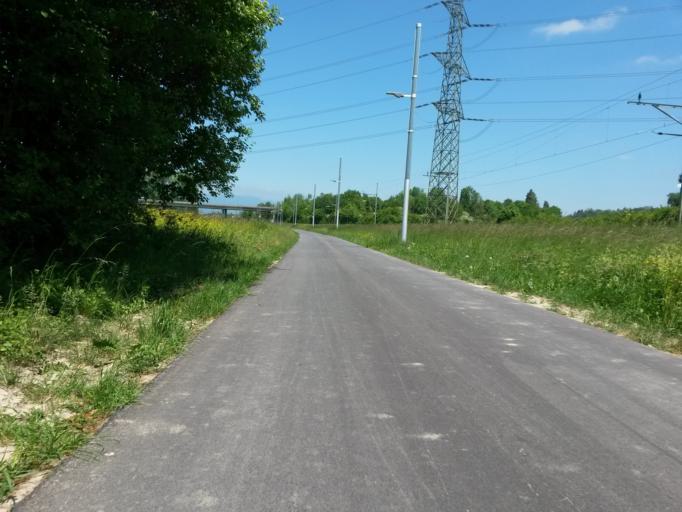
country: CH
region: Bern
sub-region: Seeland District
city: Lyss
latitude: 47.0588
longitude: 7.2934
